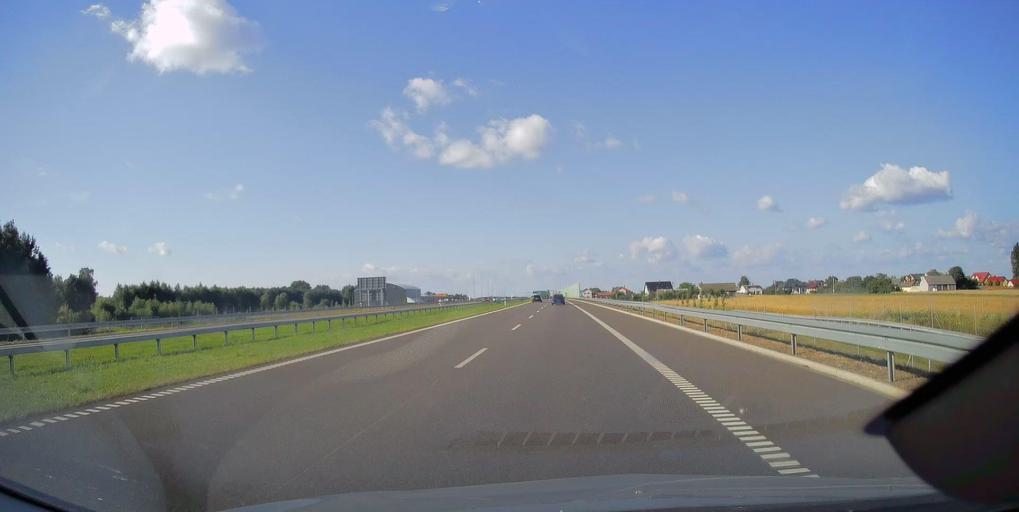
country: PL
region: Masovian Voivodeship
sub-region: Powiat radomski
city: Wolanow
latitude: 51.3802
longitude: 21.0198
